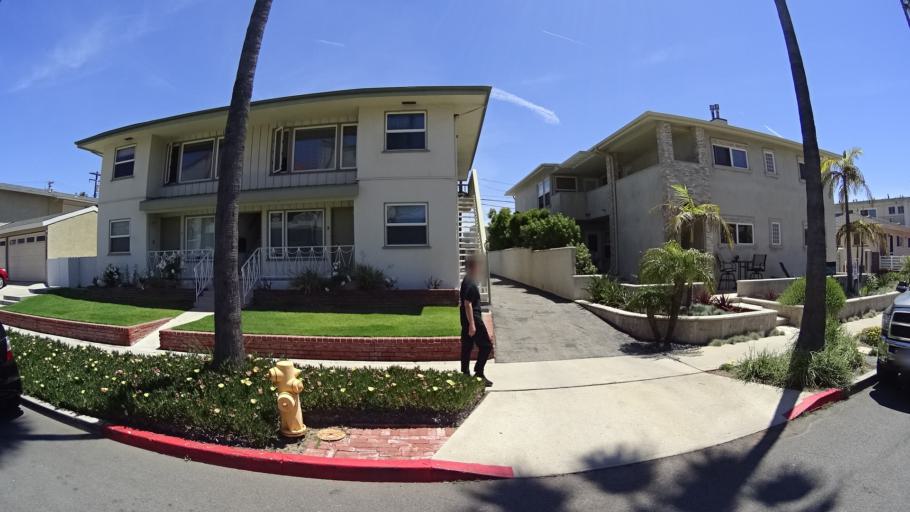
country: US
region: California
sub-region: Los Angeles County
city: Palos Verdes Estates
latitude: 33.8181
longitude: -118.3891
